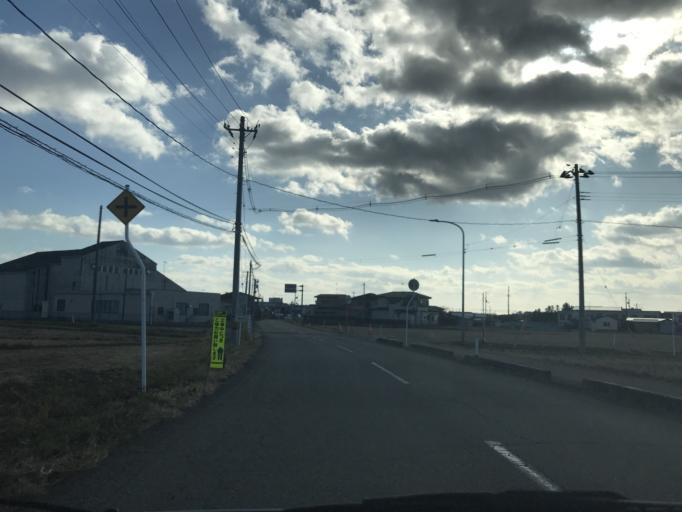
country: JP
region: Iwate
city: Ichinoseki
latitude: 38.7560
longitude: 141.0640
